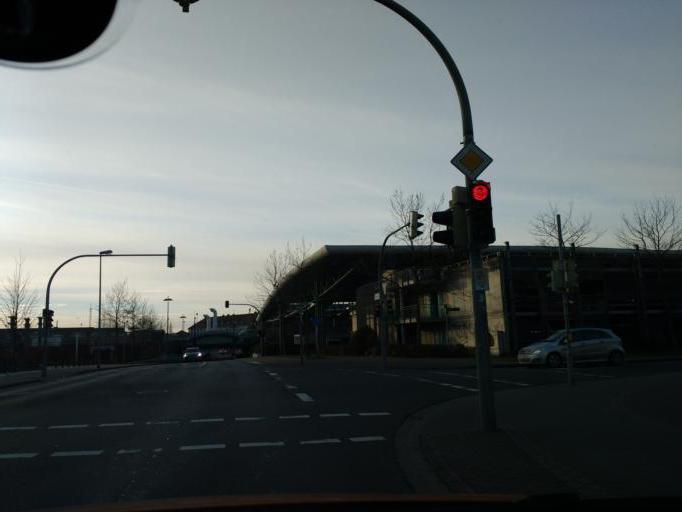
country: DE
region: Lower Saxony
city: Oldenburg
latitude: 53.1454
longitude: 8.2251
